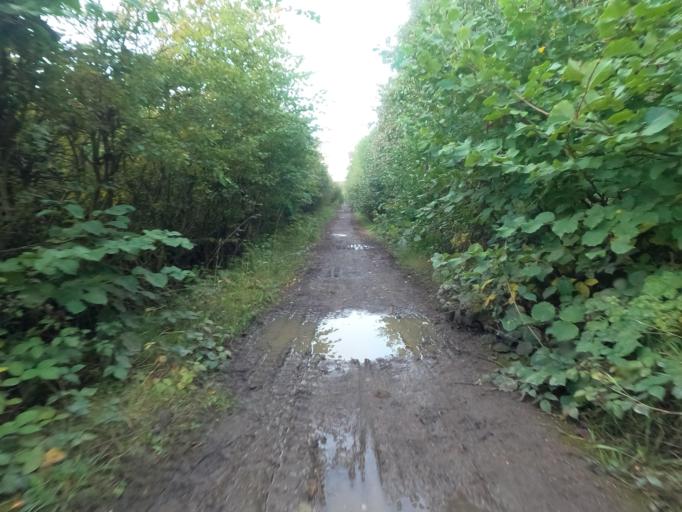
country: GB
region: England
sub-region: Northumberland
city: Seghill
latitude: 55.0716
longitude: -1.5480
